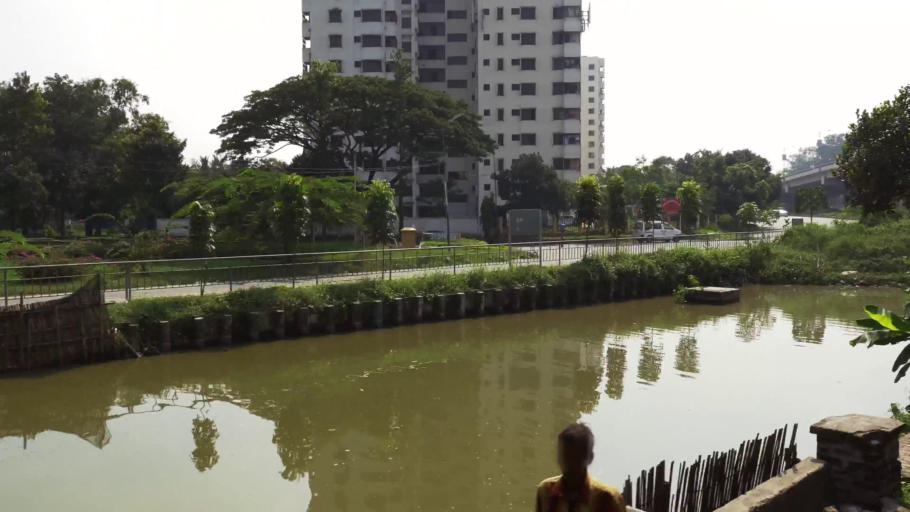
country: BD
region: Dhaka
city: Tungi
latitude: 23.8443
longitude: 90.4147
